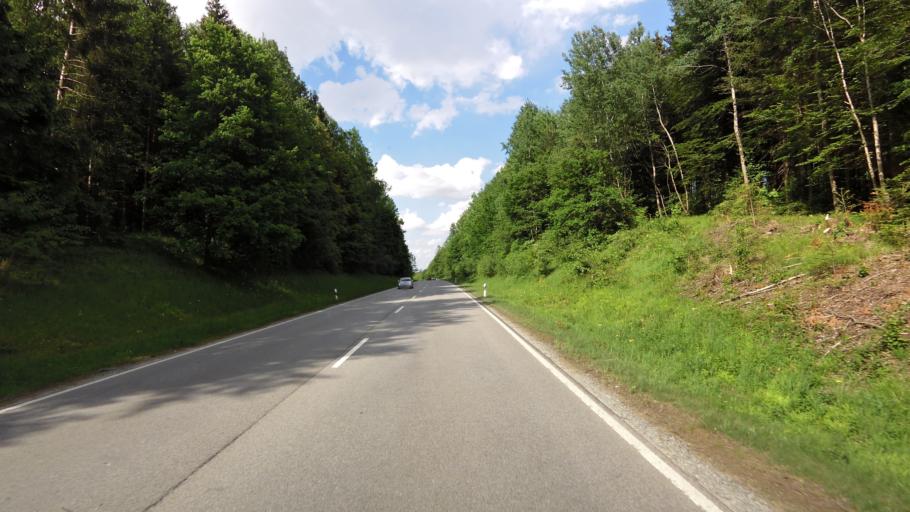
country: DE
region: Bavaria
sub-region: Upper Bavaria
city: Wasserburg am Inn
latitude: 48.0721
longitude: 12.1999
